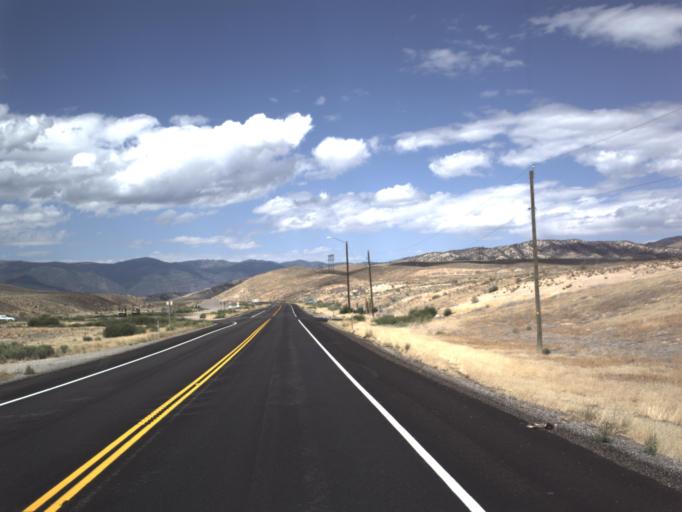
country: US
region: Utah
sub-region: Sevier County
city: Aurora
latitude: 38.9582
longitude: -111.9234
